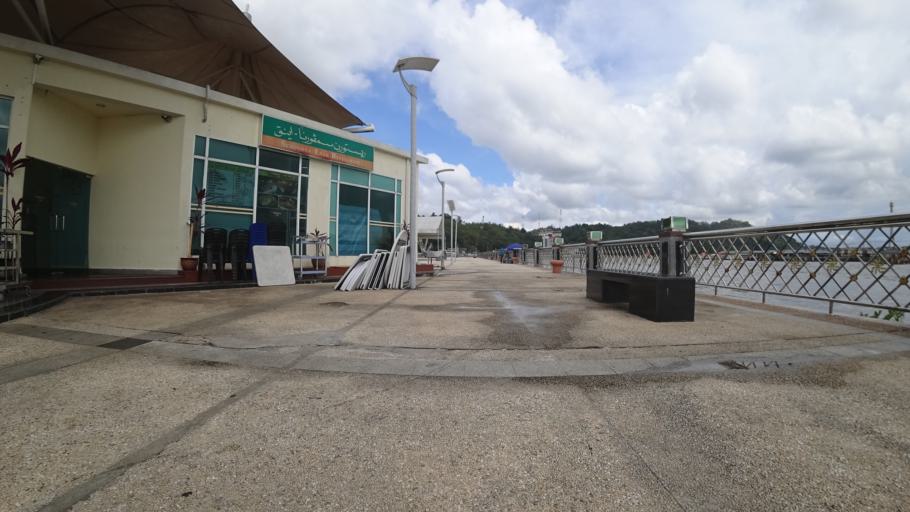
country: BN
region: Brunei and Muara
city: Bandar Seri Begawan
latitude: 4.8866
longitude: 114.9432
